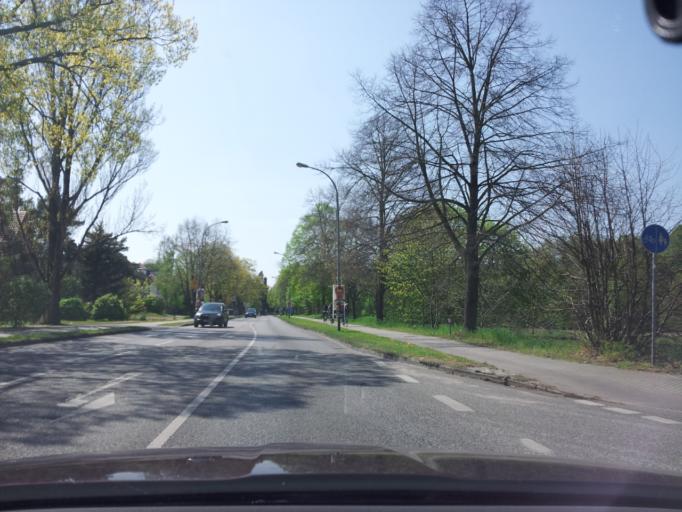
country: DE
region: Brandenburg
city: Kleinmachnow
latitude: 52.3930
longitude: 13.2344
